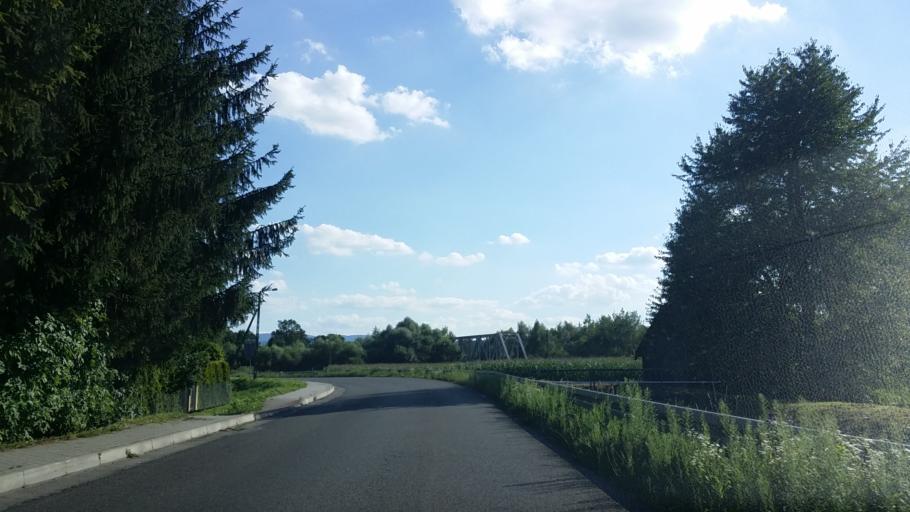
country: PL
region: Lesser Poland Voivodeship
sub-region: Powiat wadowicki
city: Wozniki
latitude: 49.9340
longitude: 19.4859
